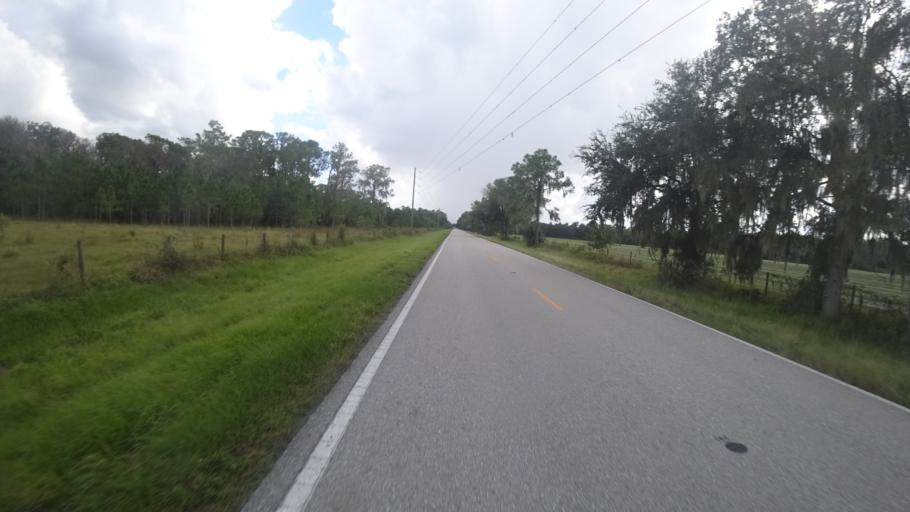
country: US
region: Florida
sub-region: Hillsborough County
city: Wimauma
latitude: 27.5699
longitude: -82.1046
